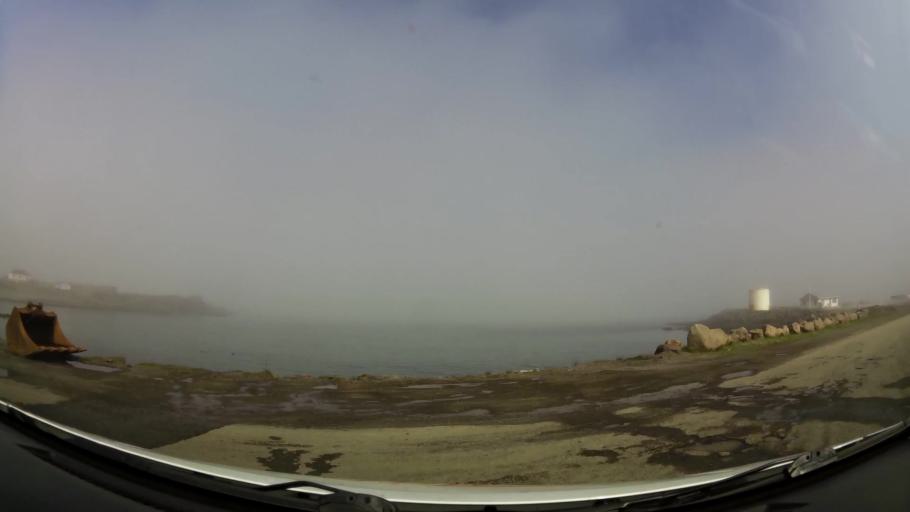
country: IS
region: East
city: Reydarfjoerdur
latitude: 64.6591
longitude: -14.2842
